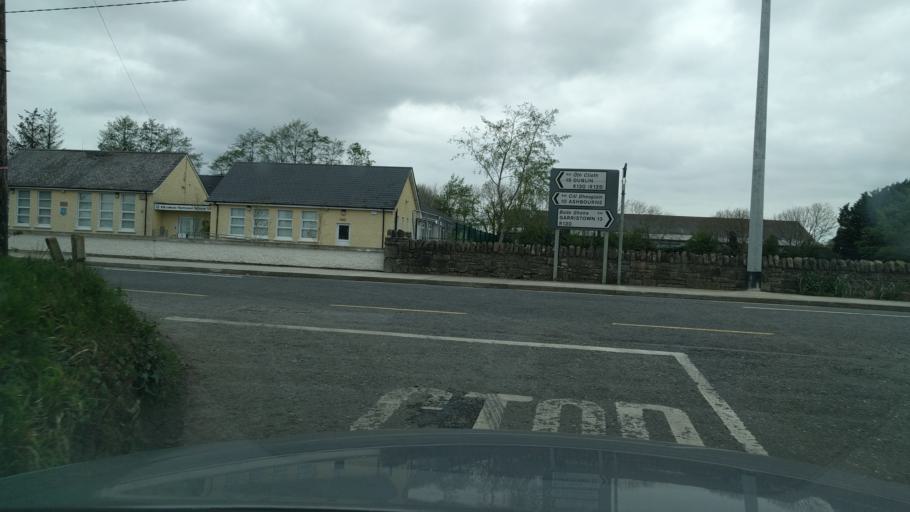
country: IE
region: Leinster
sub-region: An Mhi
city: Ashbourne
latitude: 53.4638
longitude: -6.3438
